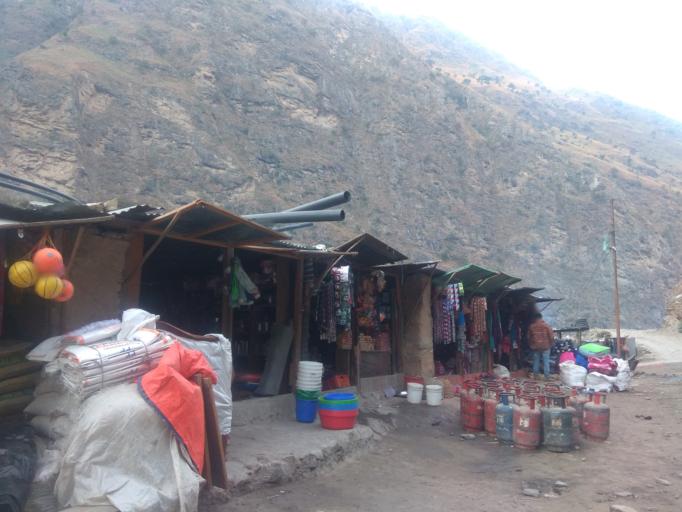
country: NP
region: Mid Western
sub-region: Bheri Zone
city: Dailekh
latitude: 29.2755
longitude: 81.7269
